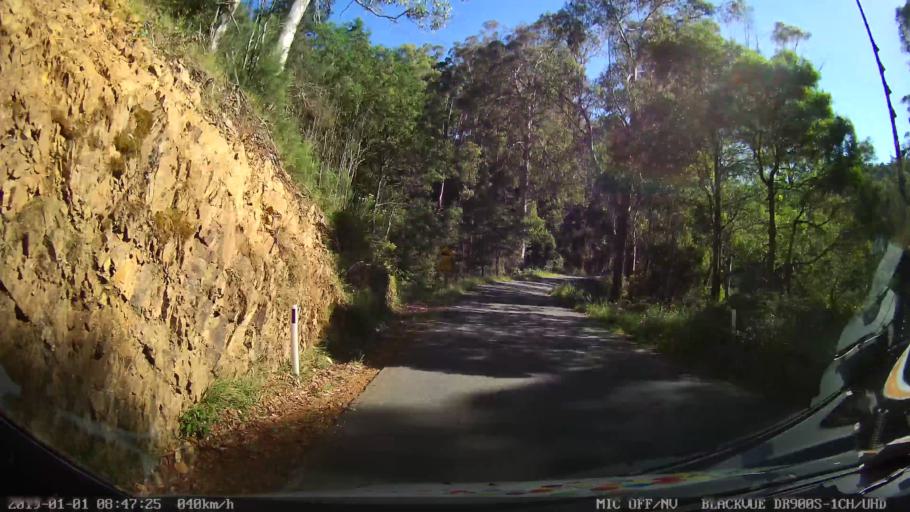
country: AU
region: New South Wales
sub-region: Snowy River
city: Jindabyne
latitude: -36.2944
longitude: 148.1969
